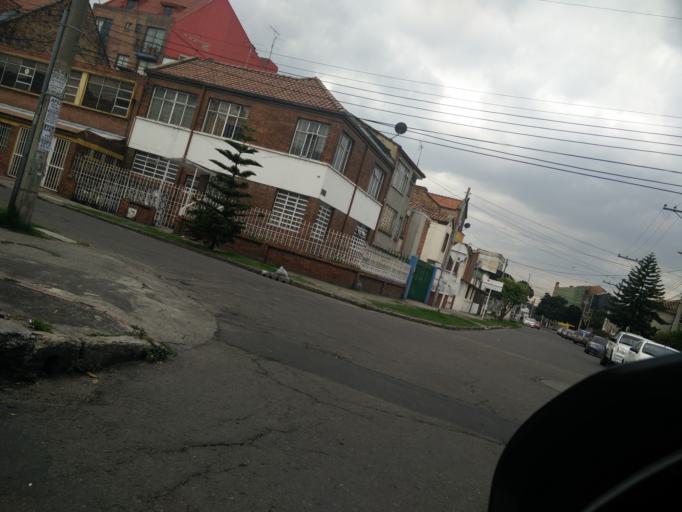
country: CO
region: Bogota D.C.
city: Bogota
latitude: 4.6519
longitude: -74.0708
